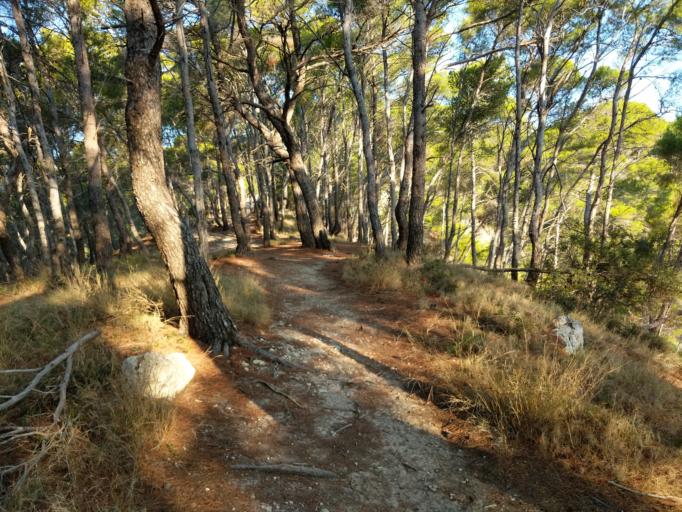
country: IT
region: Apulia
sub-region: Provincia di Foggia
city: Isole Tremiti
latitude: 42.1160
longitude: 15.4945
